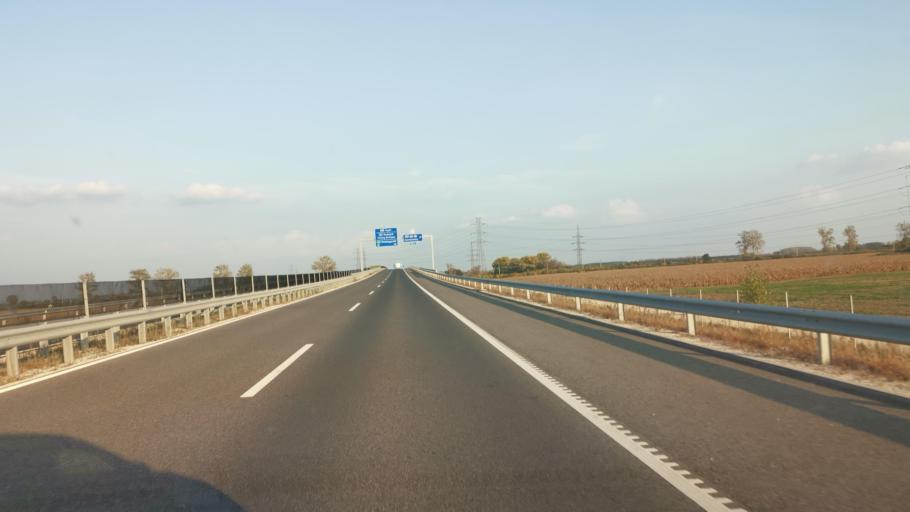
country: HU
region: Gyor-Moson-Sopron
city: Csorna
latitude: 47.5803
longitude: 17.2354
